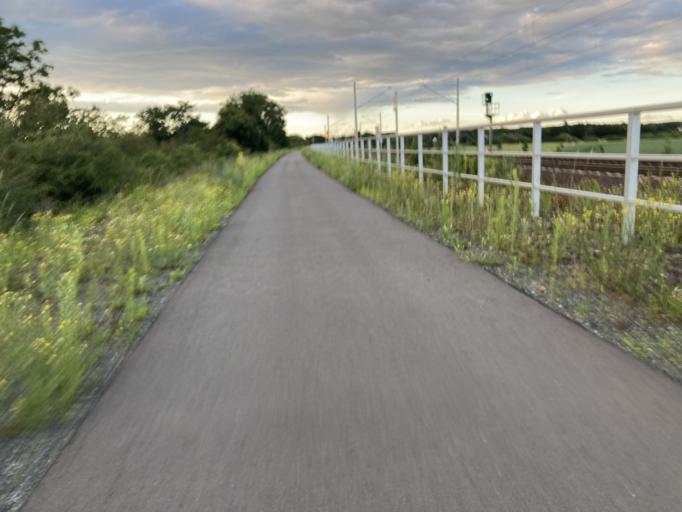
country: DE
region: Lower Saxony
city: Verden
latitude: 52.9024
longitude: 9.2393
